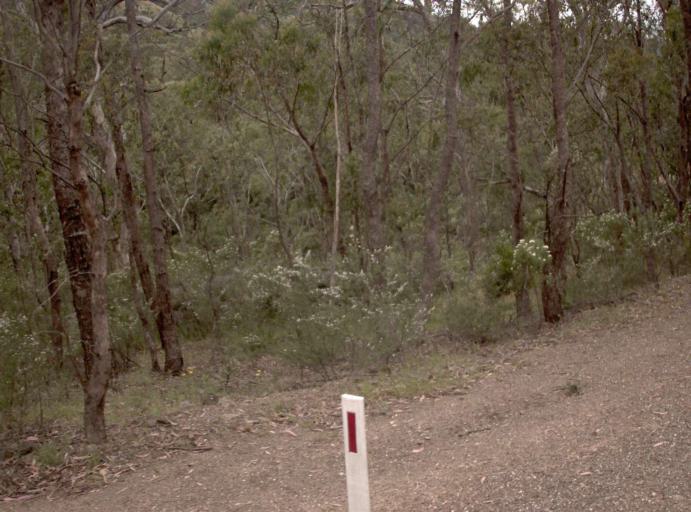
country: AU
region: Victoria
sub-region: East Gippsland
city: Bairnsdale
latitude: -37.5378
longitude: 147.2091
